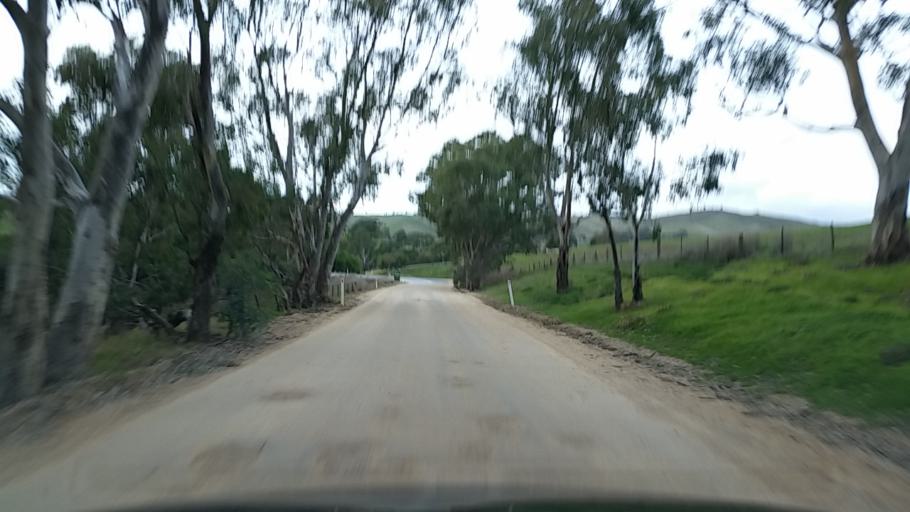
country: AU
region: South Australia
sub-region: Mount Barker
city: Nairne
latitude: -34.9532
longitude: 139.0138
